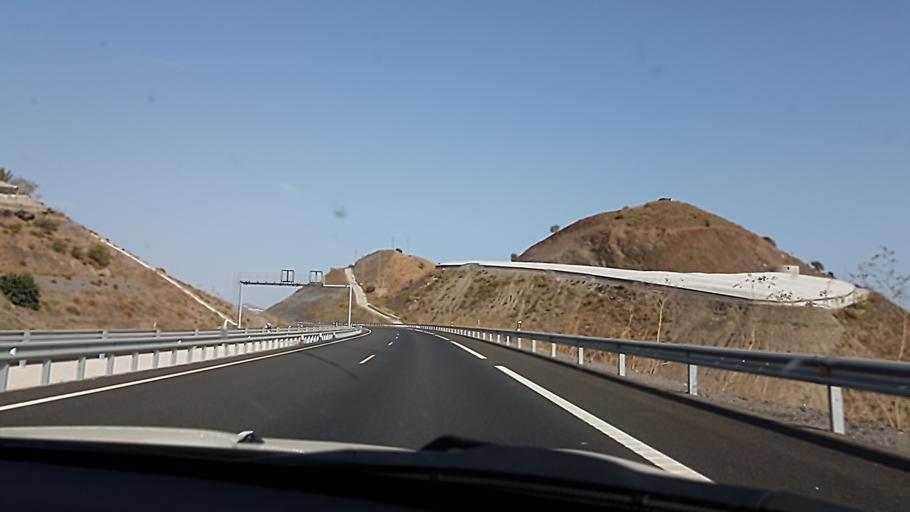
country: ES
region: Andalusia
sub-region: Provincia de Granada
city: Polopos
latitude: 36.7514
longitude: -3.2871
